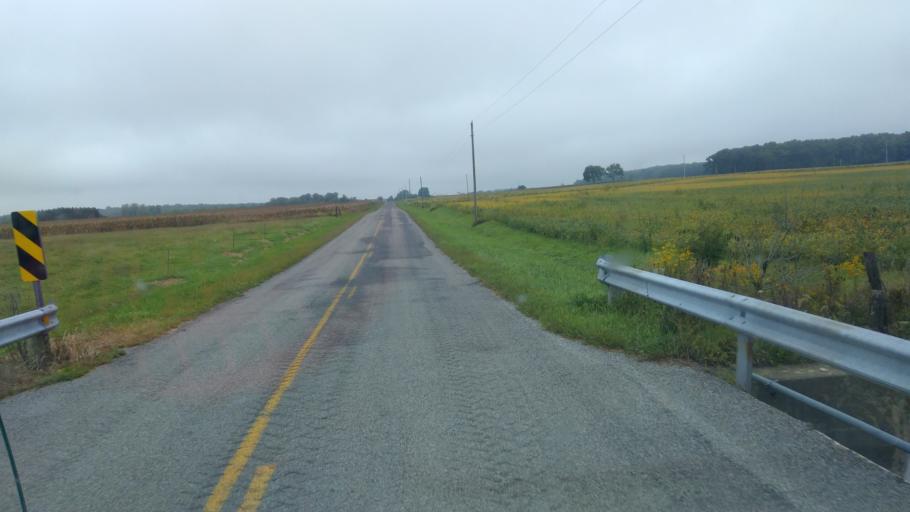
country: US
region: Ohio
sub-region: Hardin County
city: Kenton
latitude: 40.5502
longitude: -83.6349
